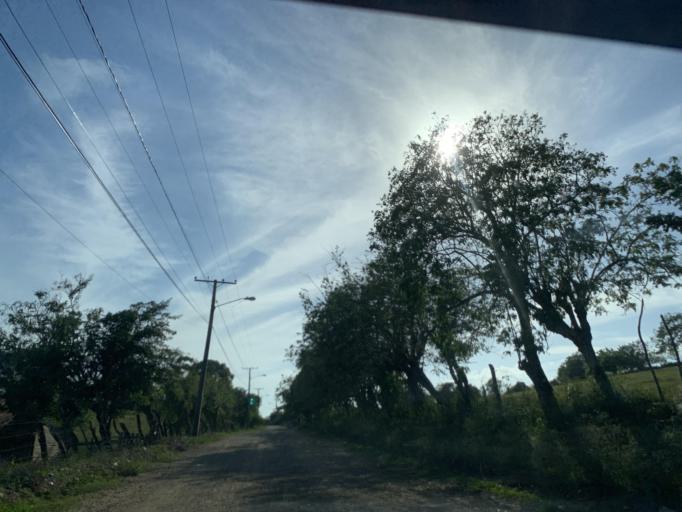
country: DO
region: Puerto Plata
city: Luperon
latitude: 19.8852
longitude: -70.9184
